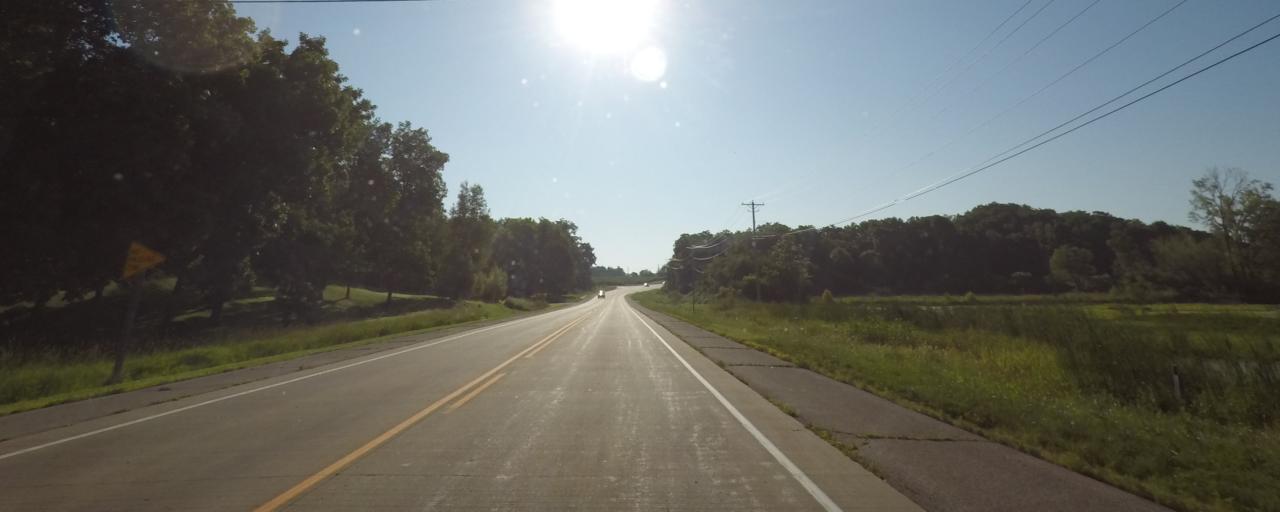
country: US
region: Wisconsin
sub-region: Jefferson County
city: Lake Ripley
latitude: 42.9876
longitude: -88.9827
